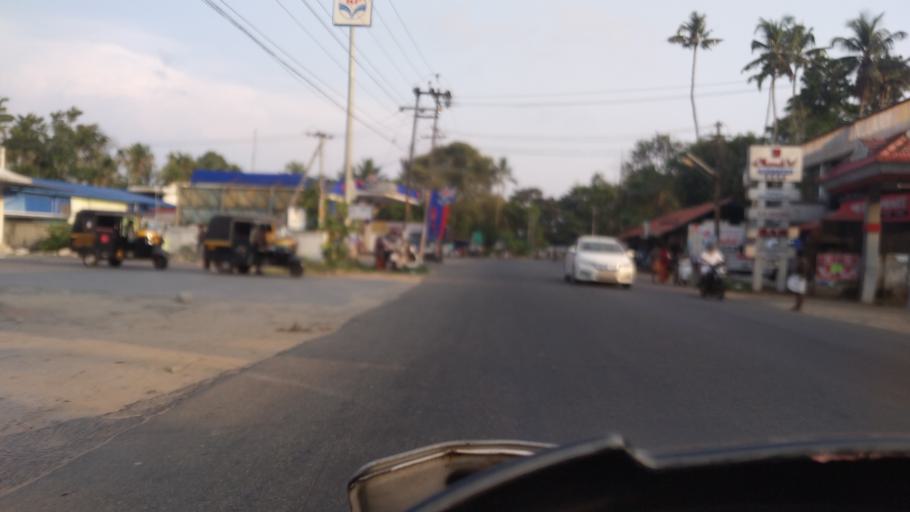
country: IN
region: Kerala
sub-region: Thrissur District
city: Irinjalakuda
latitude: 10.3232
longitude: 76.1446
